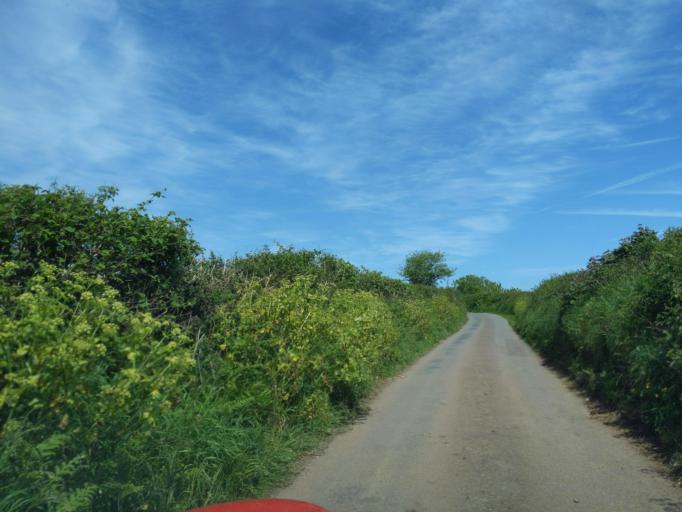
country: GB
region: England
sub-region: Devon
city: Dartmouth
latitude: 50.3576
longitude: -3.5376
